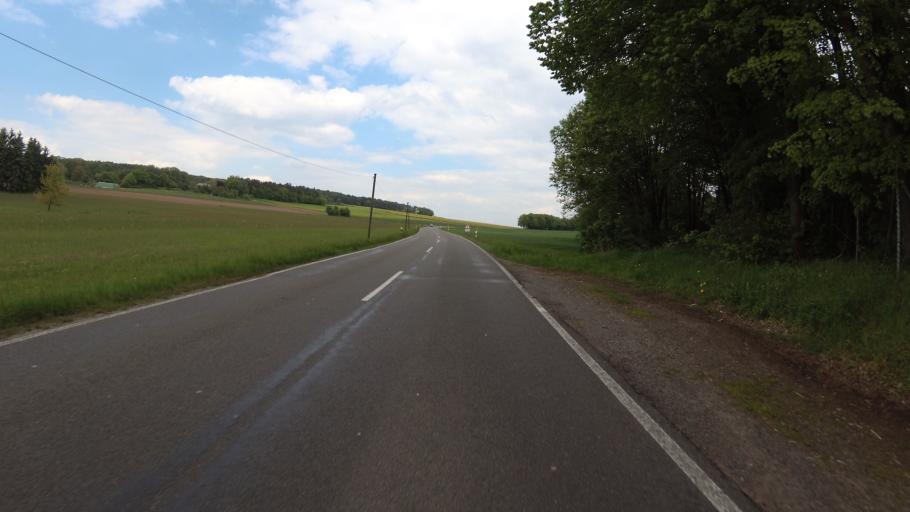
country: DE
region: Rheinland-Pfalz
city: Mackenbach
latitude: 49.4684
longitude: 7.5620
